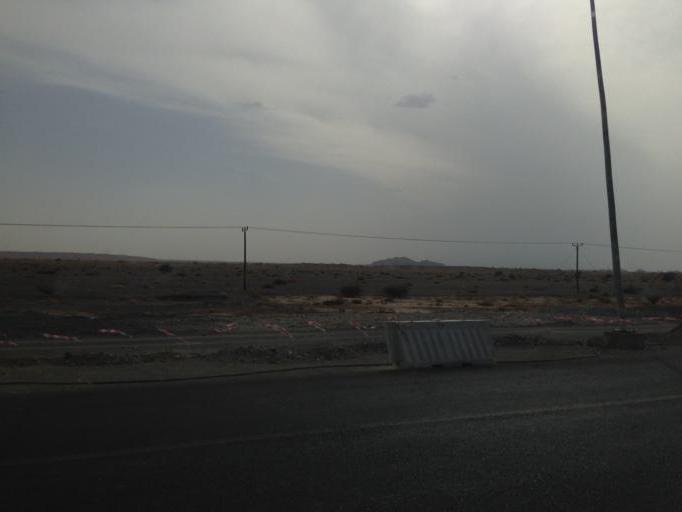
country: OM
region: Ash Sharqiyah
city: Al Qabil
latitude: 22.5488
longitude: 58.7200
